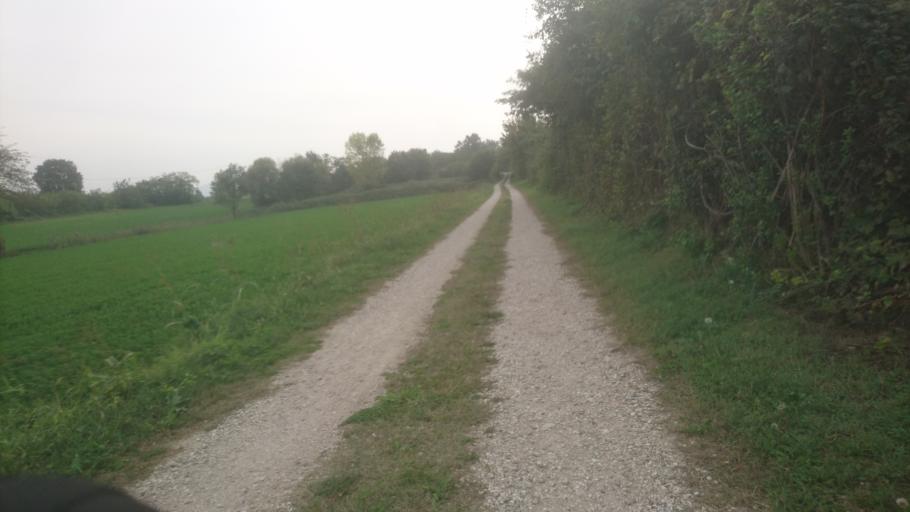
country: IT
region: Veneto
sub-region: Provincia di Vicenza
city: Montegalda
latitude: 45.4437
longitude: 11.6817
